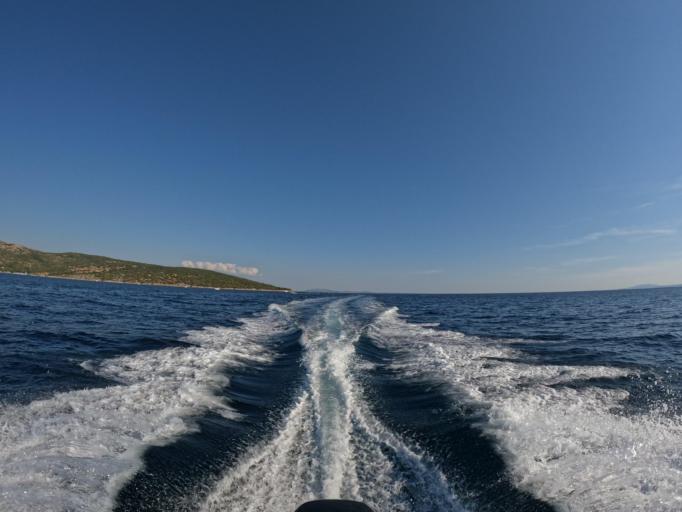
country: HR
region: Primorsko-Goranska
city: Punat
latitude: 44.9909
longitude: 14.6058
